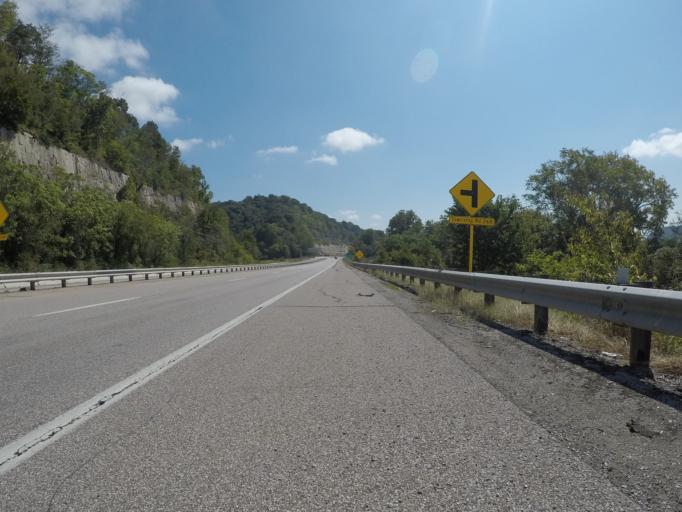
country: US
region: Kentucky
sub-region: Boyd County
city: Ashland
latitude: 38.4816
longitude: -82.6261
